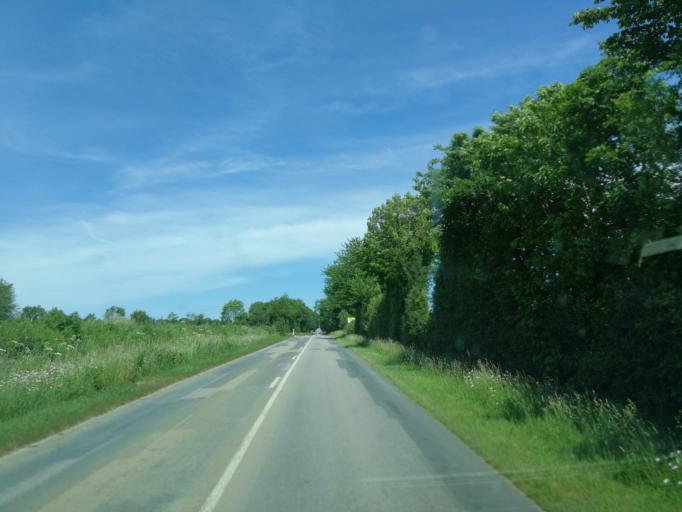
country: FR
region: Poitou-Charentes
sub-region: Departement des Deux-Sevres
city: Courlay
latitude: 46.7984
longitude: -0.5879
